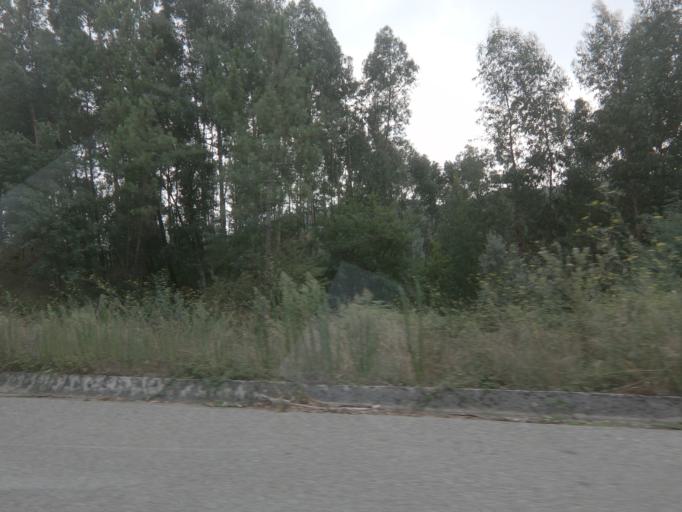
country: PT
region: Coimbra
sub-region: Penacova
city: Lorvao
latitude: 40.2953
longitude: -8.3092
